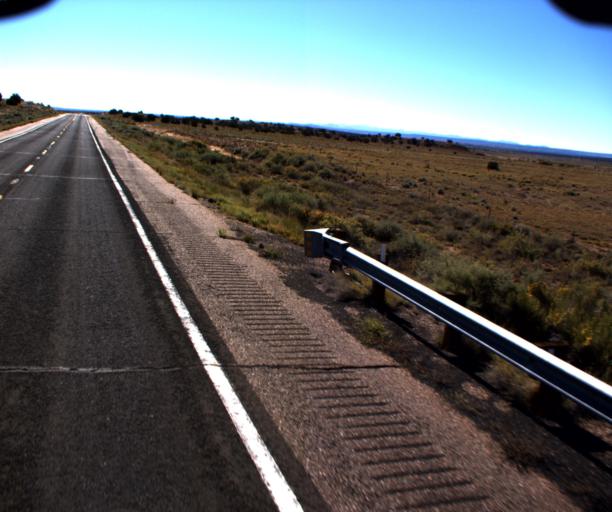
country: US
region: Arizona
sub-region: Navajo County
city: Snowflake
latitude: 34.6780
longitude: -109.7319
